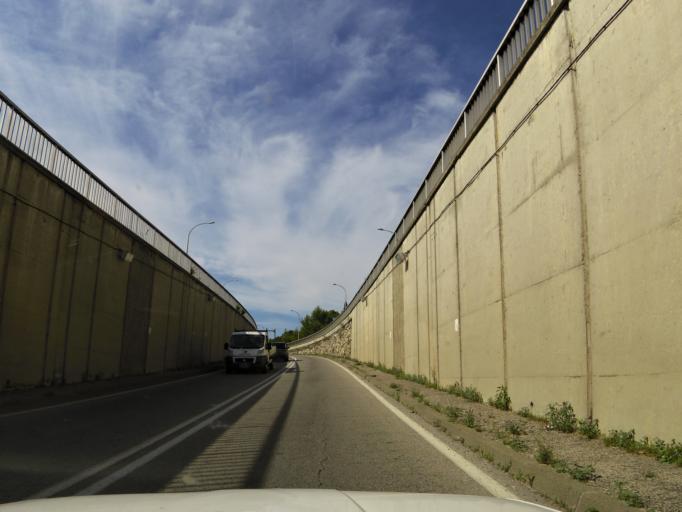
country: FR
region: Languedoc-Roussillon
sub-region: Departement du Gard
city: Nimes
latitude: 43.8400
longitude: 4.3195
